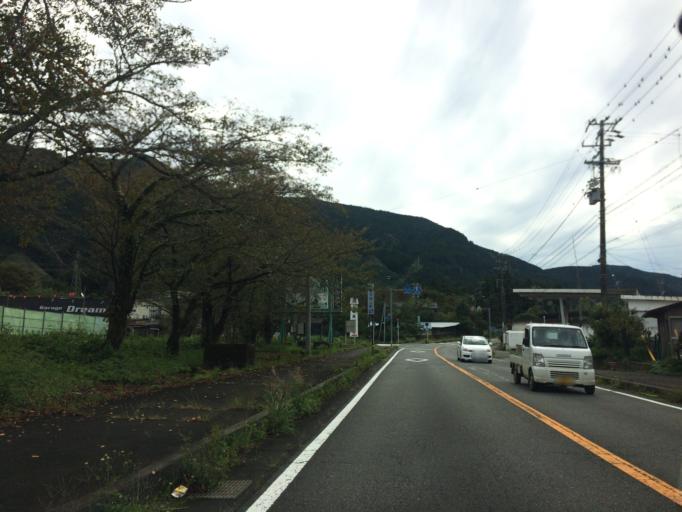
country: JP
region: Shizuoka
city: Kanaya
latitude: 35.0746
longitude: 138.1104
